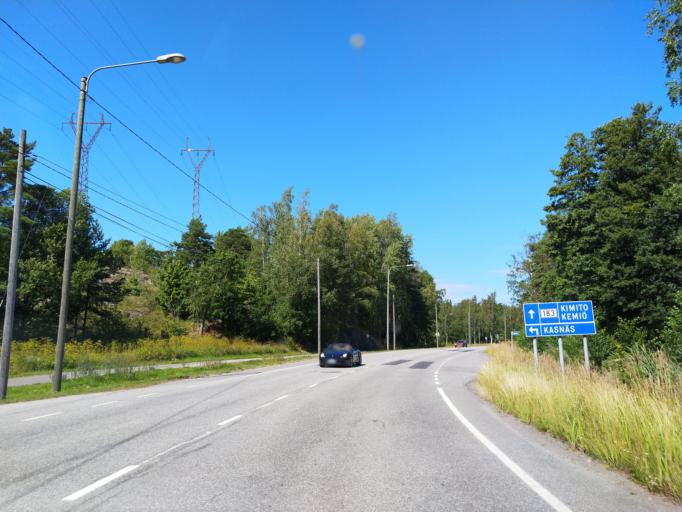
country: FI
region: Varsinais-Suomi
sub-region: Aboland-Turunmaa
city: Dragsfjaerd
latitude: 60.0187
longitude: 22.4974
